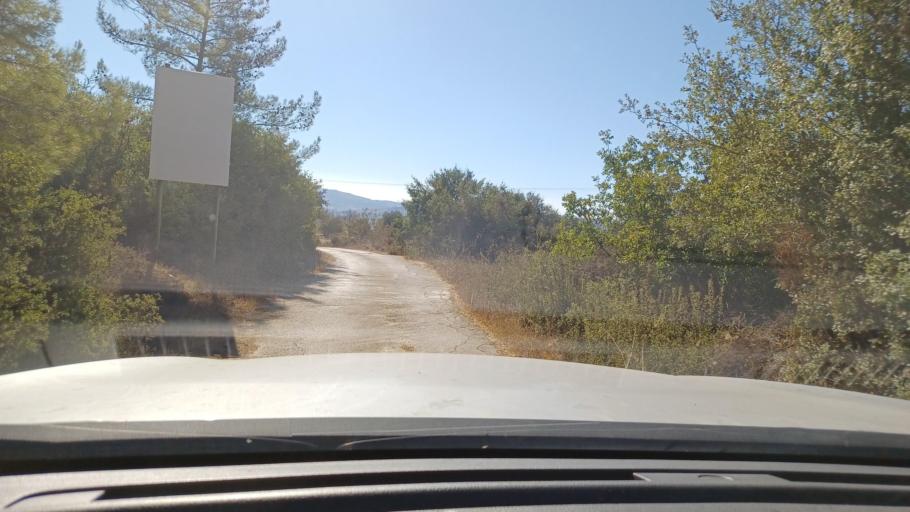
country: CY
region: Pafos
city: Polis
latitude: 34.9893
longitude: 32.5185
